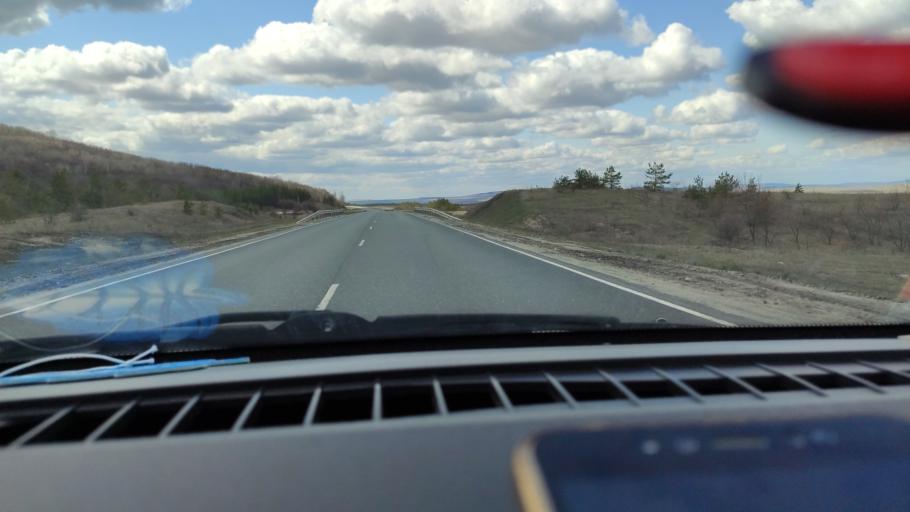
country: RU
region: Saratov
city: Alekseyevka
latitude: 52.3931
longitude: 47.9790
